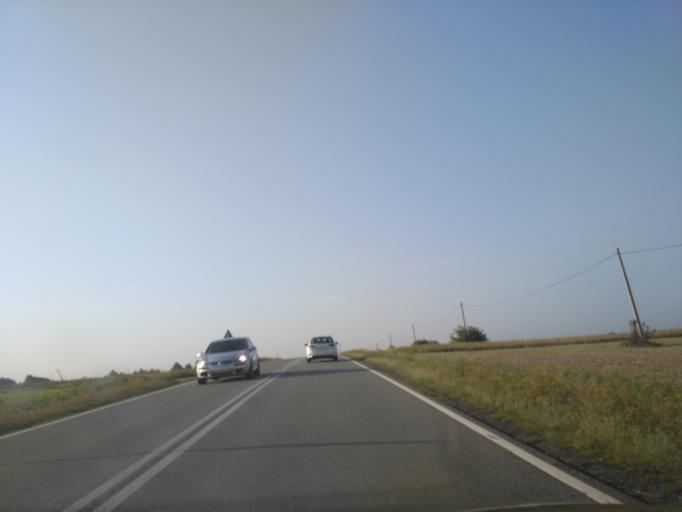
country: PL
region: Lublin Voivodeship
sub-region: Powiat janowski
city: Modliborzyce
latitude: 50.7795
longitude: 22.3237
